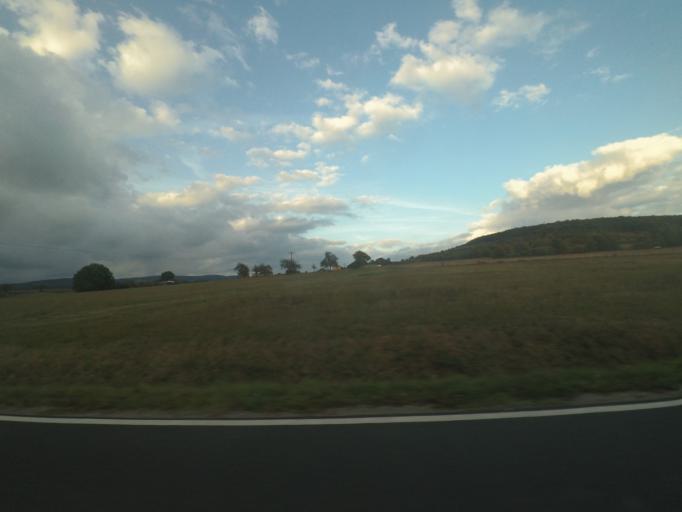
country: DE
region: Bavaria
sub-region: Regierungsbezirk Unterfranken
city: Schondra
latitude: 50.2629
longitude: 9.8620
